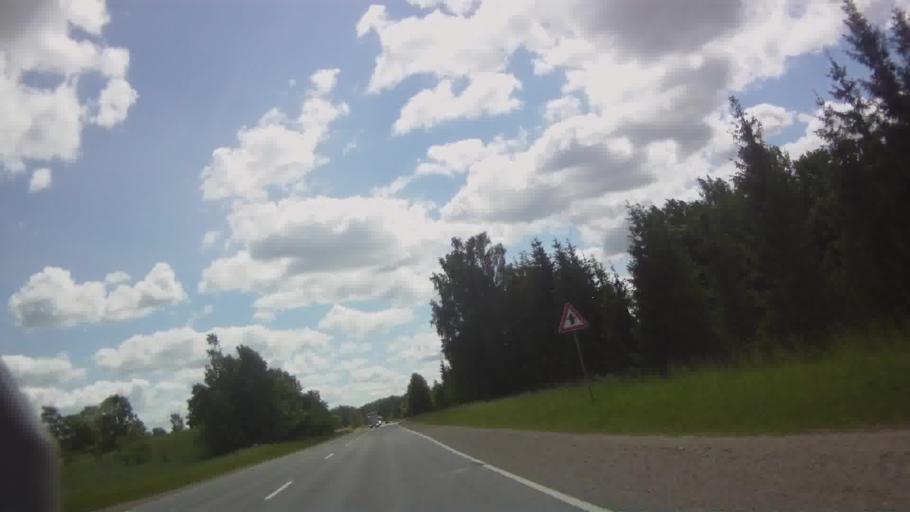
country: LV
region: Vilanu
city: Vilani
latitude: 56.5921
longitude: 26.8804
